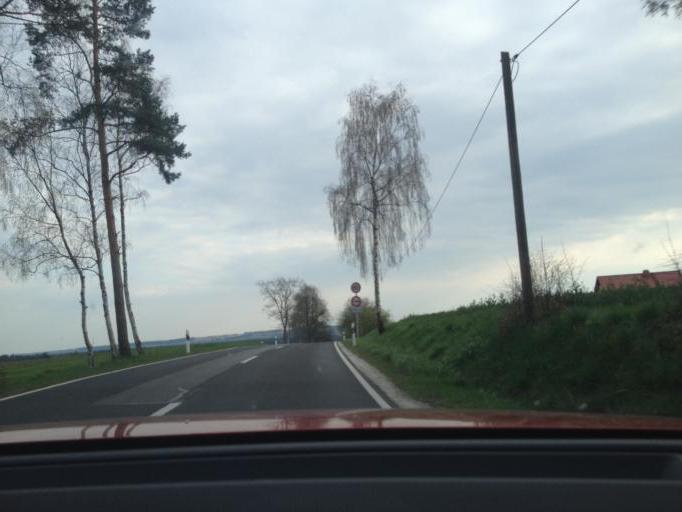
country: DE
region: Bavaria
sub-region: Upper Palatinate
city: Speinshart
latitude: 49.7939
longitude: 11.8205
